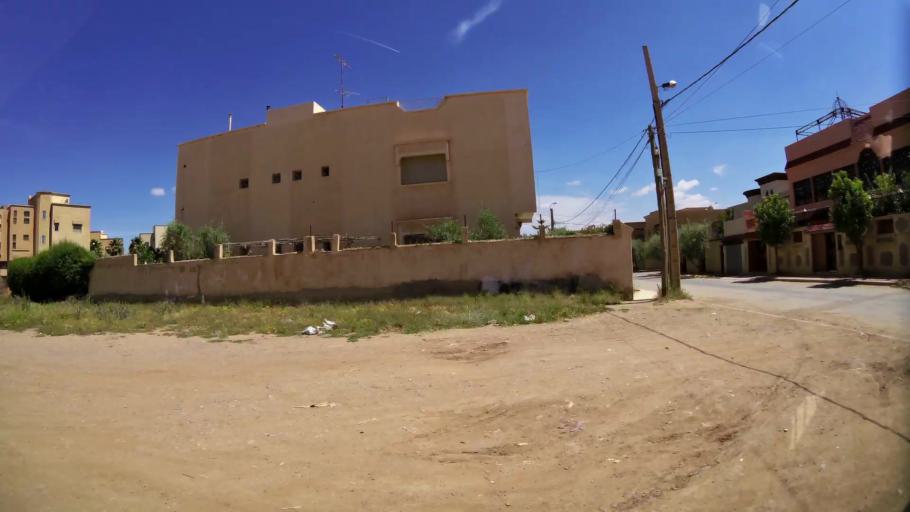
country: MA
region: Oriental
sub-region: Oujda-Angad
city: Oujda
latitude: 34.6640
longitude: -1.9312
